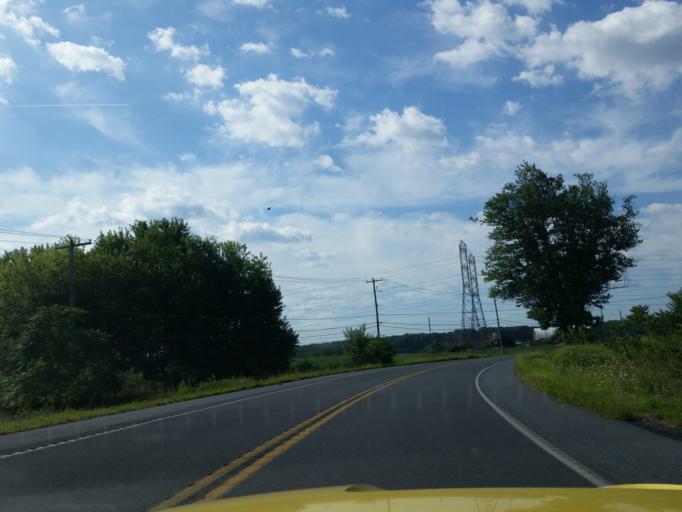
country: US
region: Pennsylvania
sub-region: Lebanon County
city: Sand Hill
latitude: 40.3850
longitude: -76.4109
